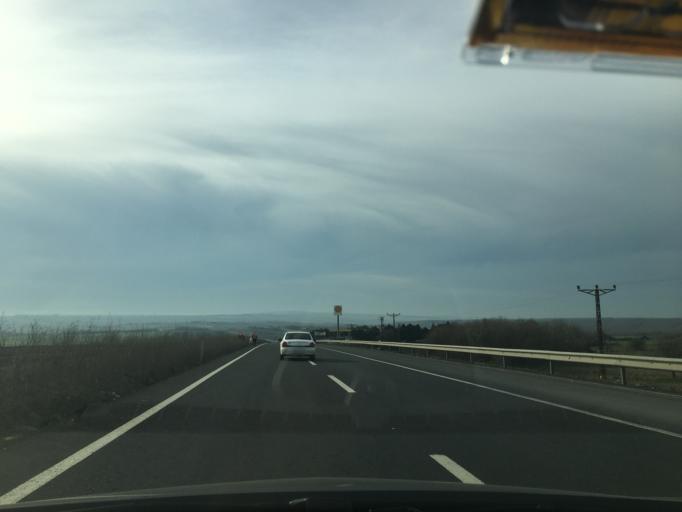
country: TR
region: Istanbul
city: Buyukcavuslu
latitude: 41.2588
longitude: 28.0362
